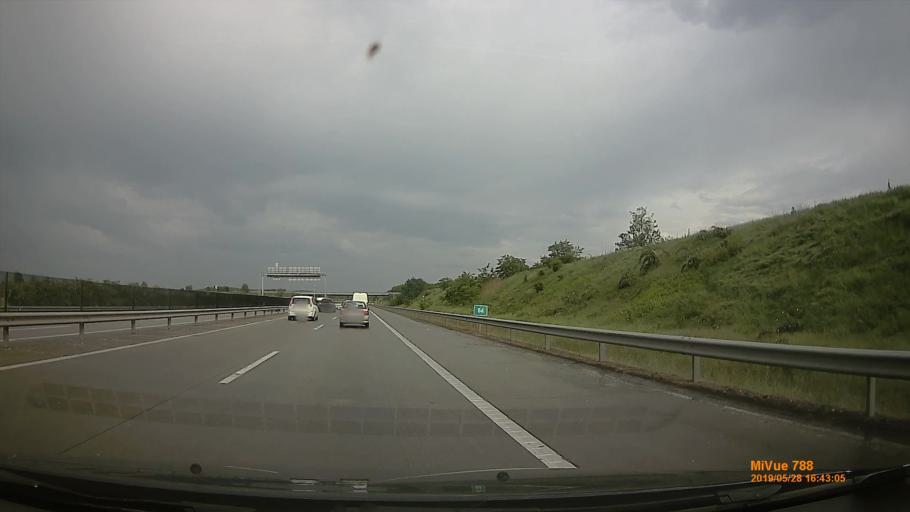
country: HU
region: Pest
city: Csomor
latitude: 47.5470
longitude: 19.1948
